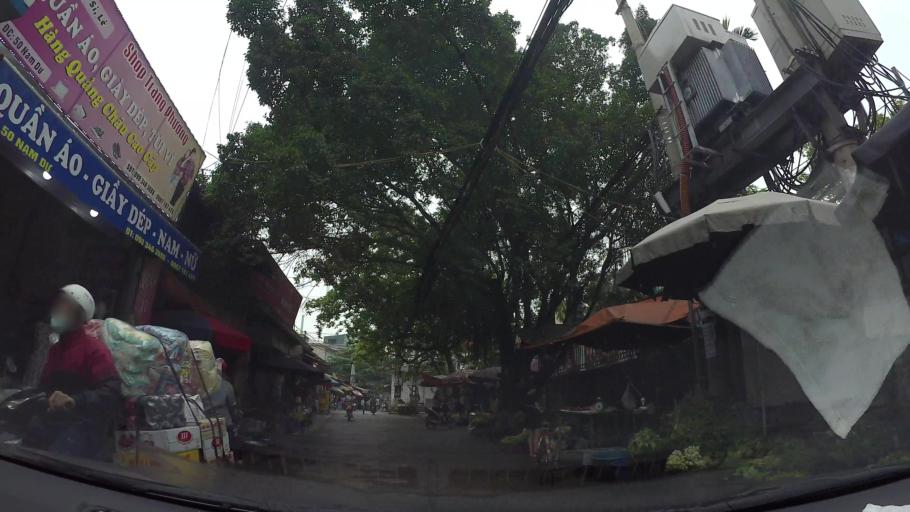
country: VN
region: Ha Noi
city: Hai BaTrung
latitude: 20.9861
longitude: 105.8885
